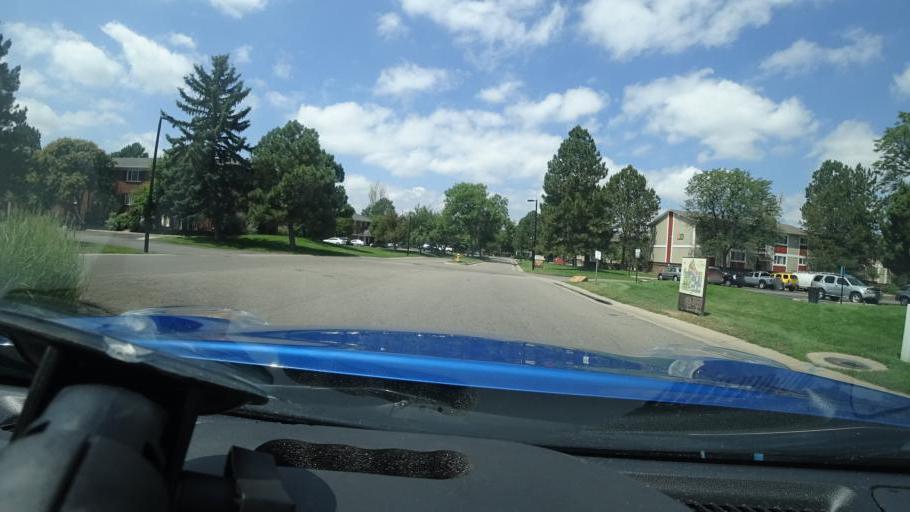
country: US
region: Colorado
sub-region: Adams County
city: Aurora
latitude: 39.7159
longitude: -104.8475
